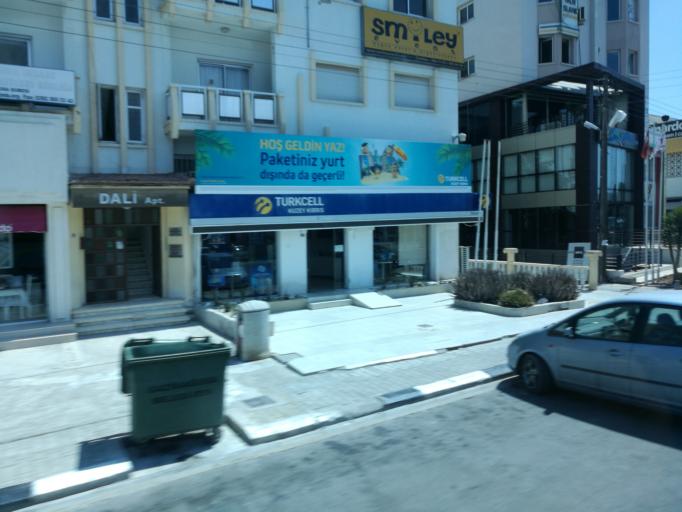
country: CY
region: Ammochostos
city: Famagusta
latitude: 35.1313
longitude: 33.9259
